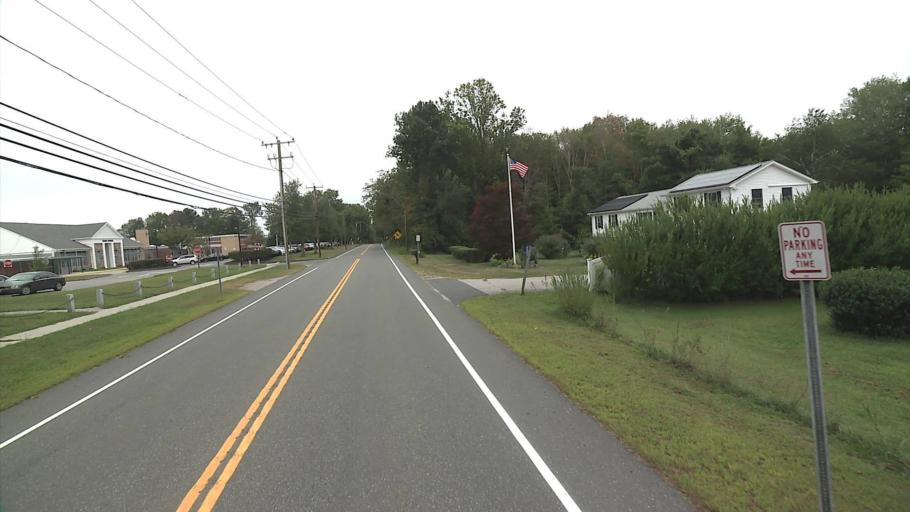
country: US
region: Connecticut
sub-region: New London County
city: Colchester
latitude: 41.4887
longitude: -72.2752
